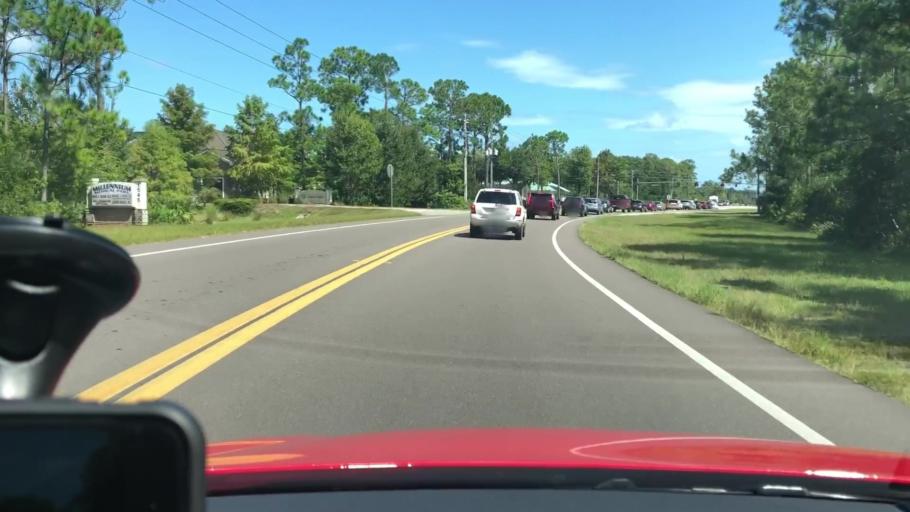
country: US
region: Florida
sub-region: Volusia County
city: Ormond Beach
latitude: 29.2617
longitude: -81.0965
